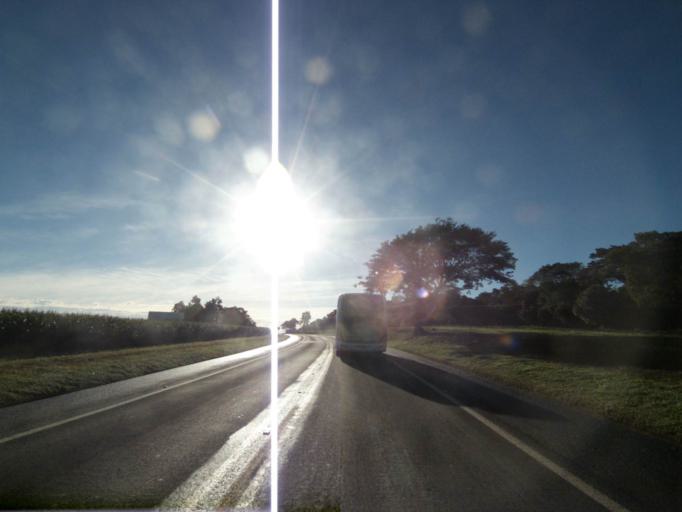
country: BR
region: Parana
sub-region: Matelandia
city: Matelandia
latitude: -25.1125
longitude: -53.7690
